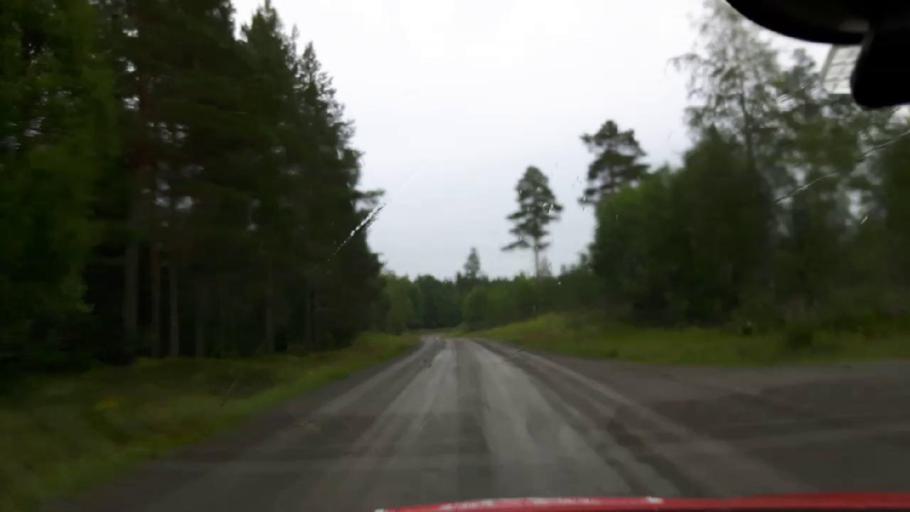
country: SE
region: Jaemtland
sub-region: OEstersunds Kommun
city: Brunflo
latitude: 62.9796
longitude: 14.8272
